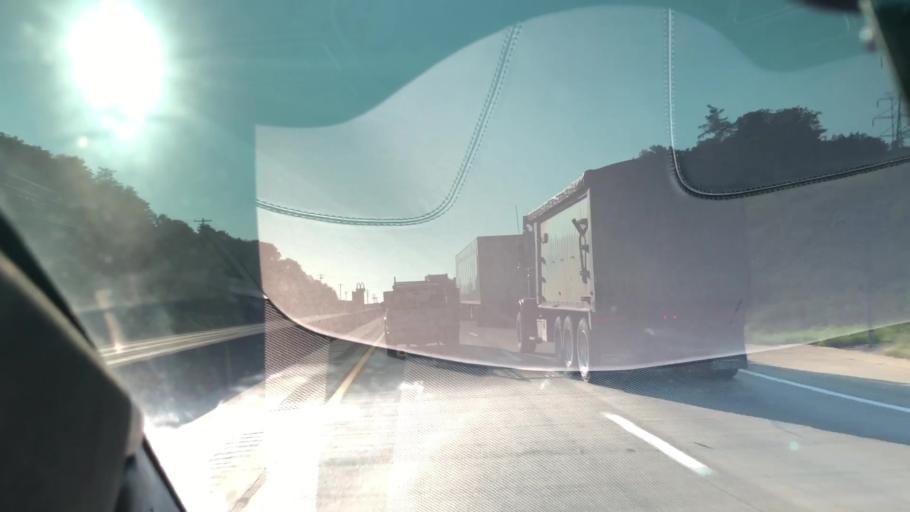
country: US
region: Pennsylvania
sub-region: Westmoreland County
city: Delmont
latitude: 40.4019
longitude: -79.5911
